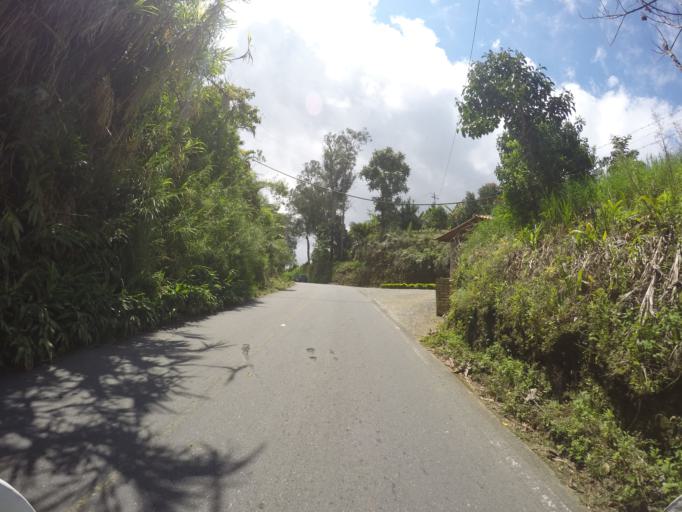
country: CO
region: Quindio
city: Filandia
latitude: 4.6534
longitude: -75.6768
